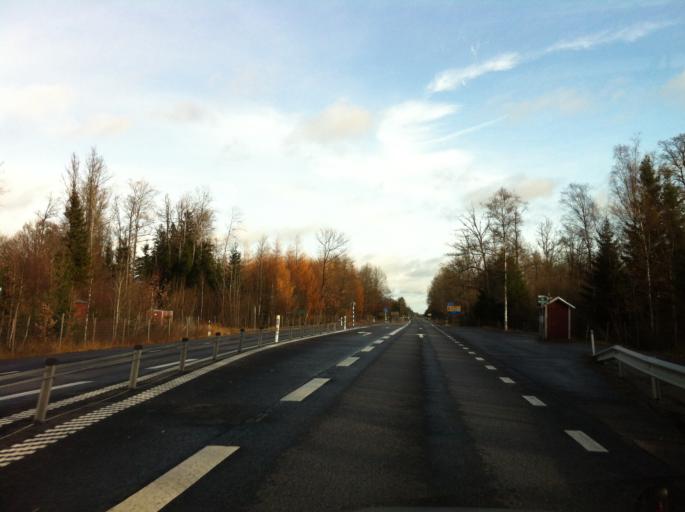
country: SE
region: Kronoberg
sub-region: Alvesta Kommun
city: Vislanda
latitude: 56.6862
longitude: 14.3210
